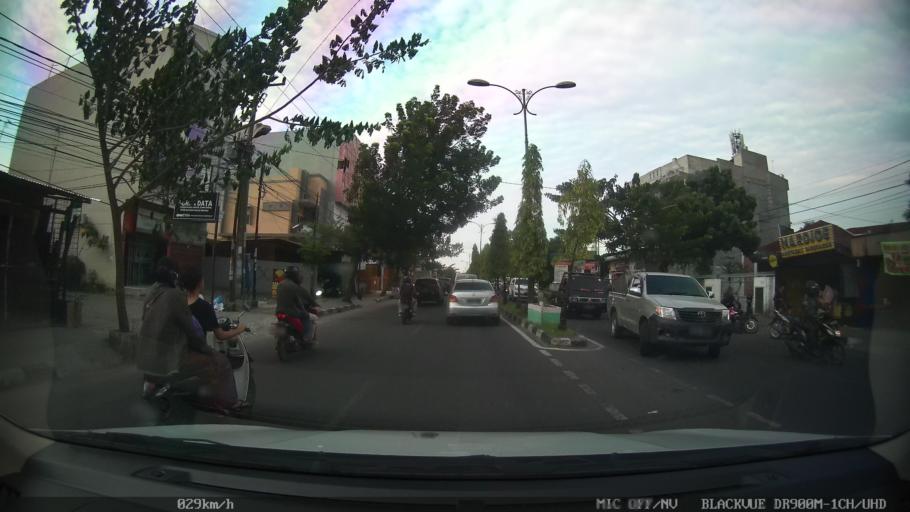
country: ID
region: North Sumatra
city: Sunggal
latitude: 3.5595
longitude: 98.6357
